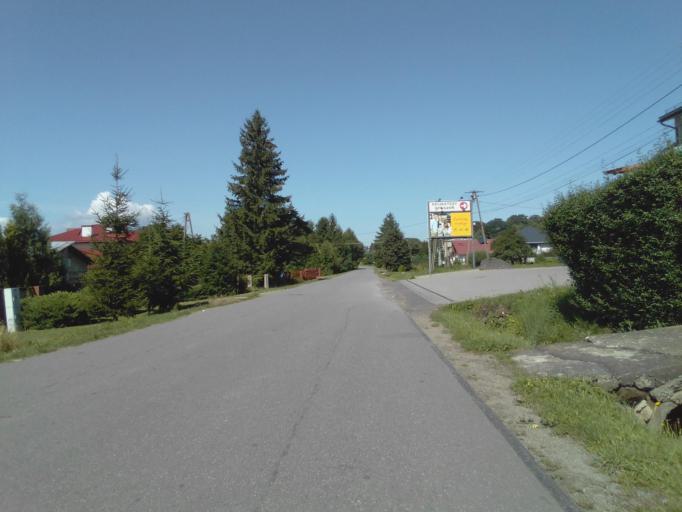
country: PL
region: Subcarpathian Voivodeship
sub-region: Powiat krosnienski
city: Chorkowka
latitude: 49.6059
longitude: 21.6540
